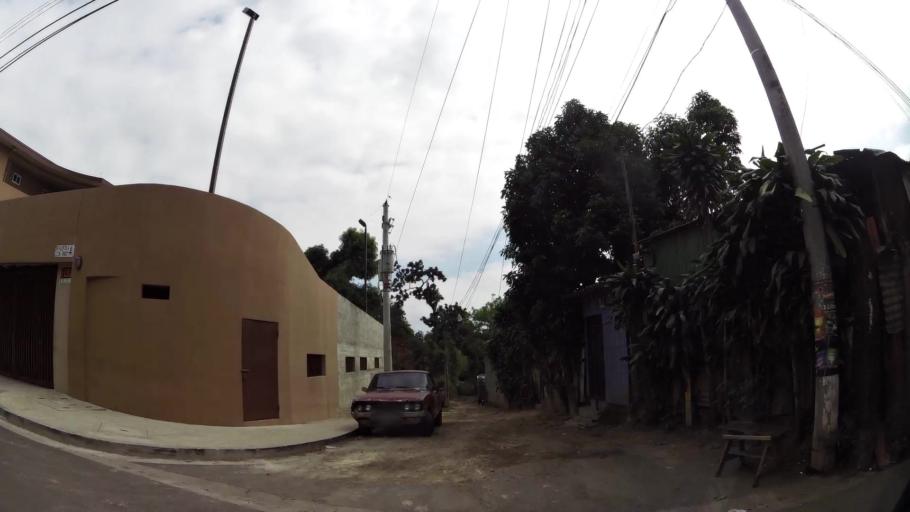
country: SV
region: La Libertad
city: Santa Tecla
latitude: 13.7088
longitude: -89.2623
